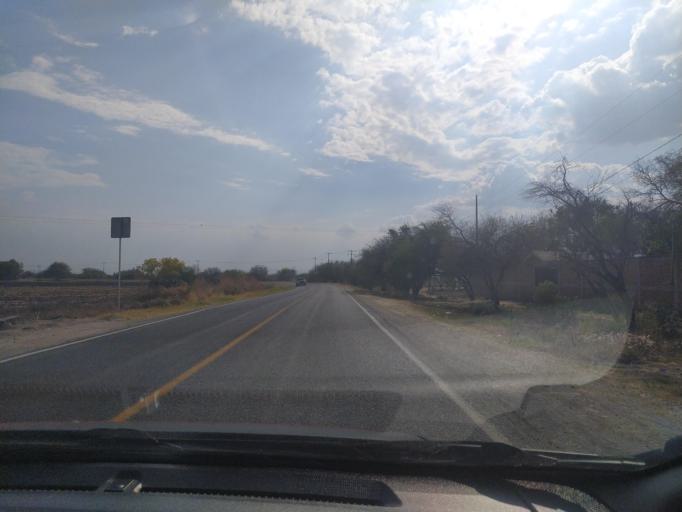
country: MX
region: Guanajuato
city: San Roque
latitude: 20.9448
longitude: -101.8550
